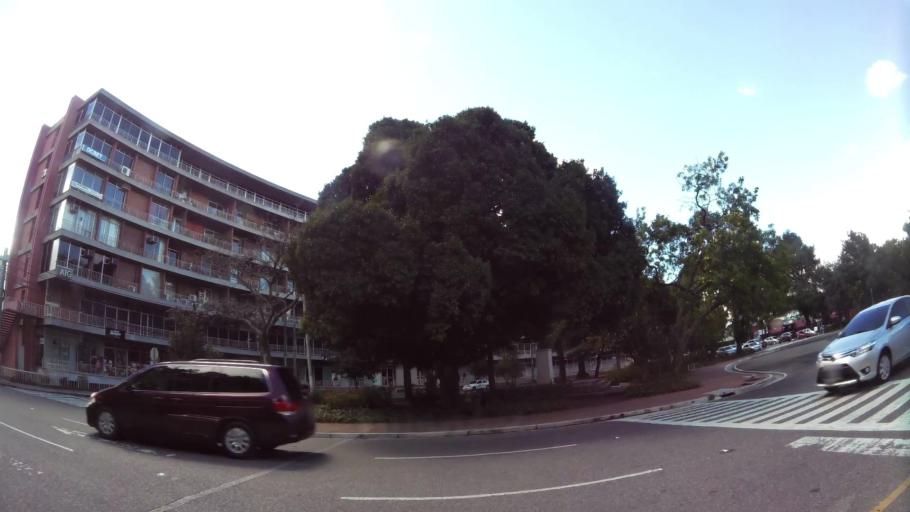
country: GT
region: Guatemala
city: Santa Catarina Pinula
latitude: 14.6012
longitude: -90.5184
